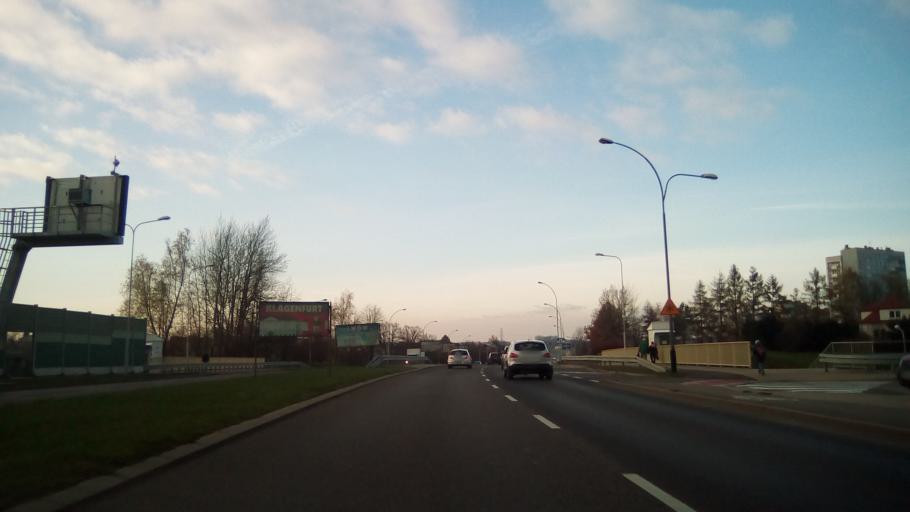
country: PL
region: Subcarpathian Voivodeship
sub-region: Rzeszow
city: Rzeszow
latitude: 50.0485
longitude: 21.9753
